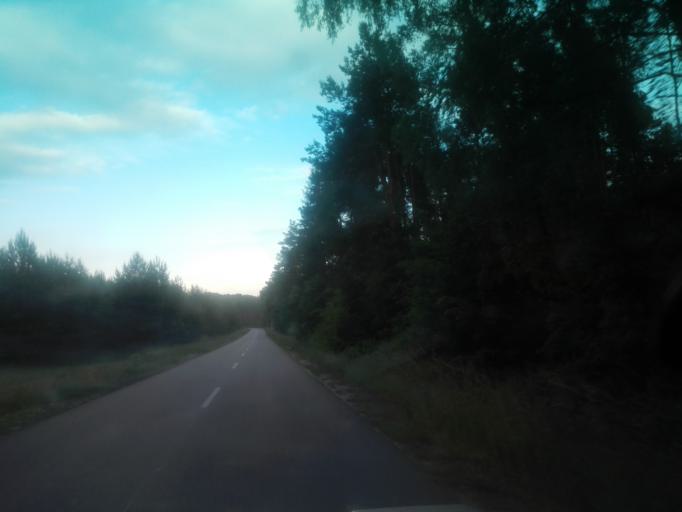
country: PL
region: Silesian Voivodeship
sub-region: Powiat czestochowski
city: Potok Zloty
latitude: 50.6928
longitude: 19.3889
